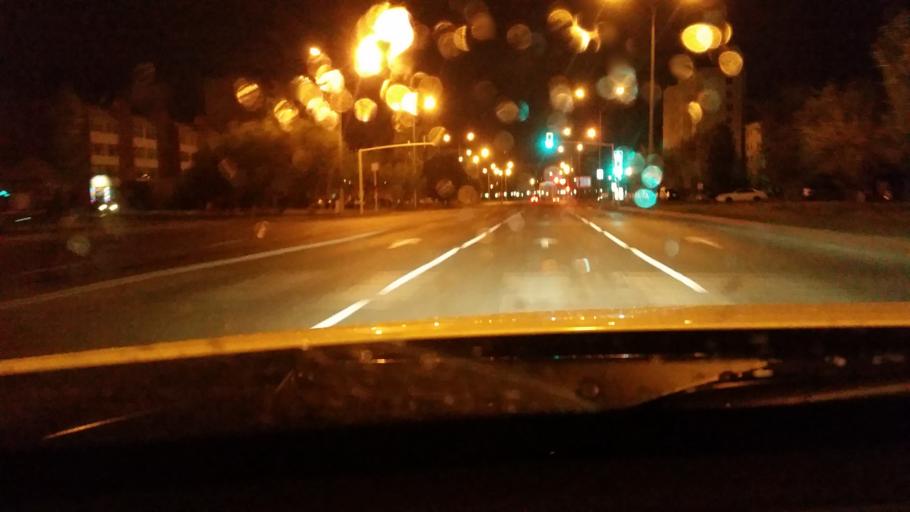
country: KZ
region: Astana Qalasy
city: Astana
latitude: 51.1542
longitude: 71.4793
